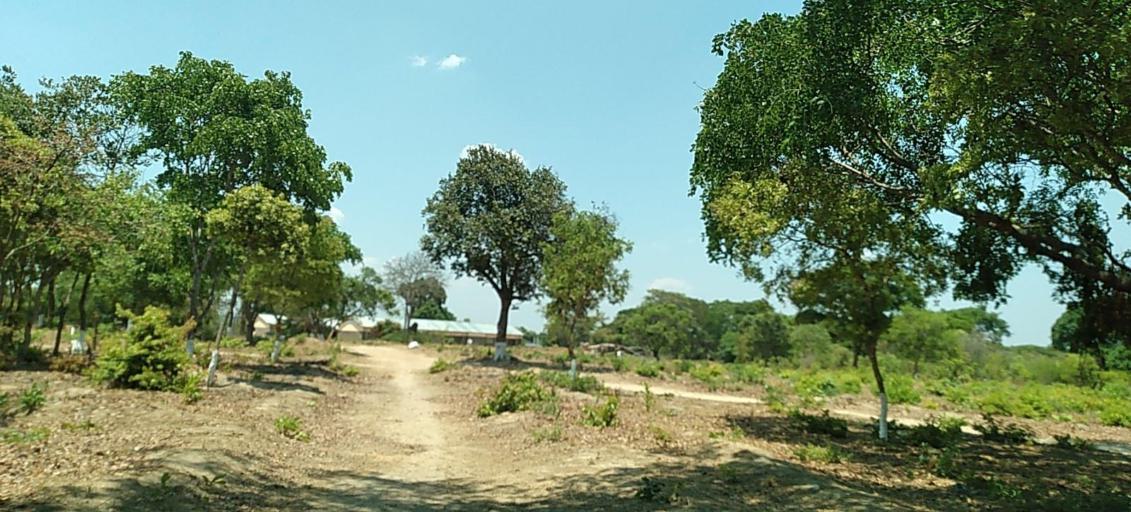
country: ZM
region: Central
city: Kapiri Mposhi
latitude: -13.6738
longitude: 28.5030
